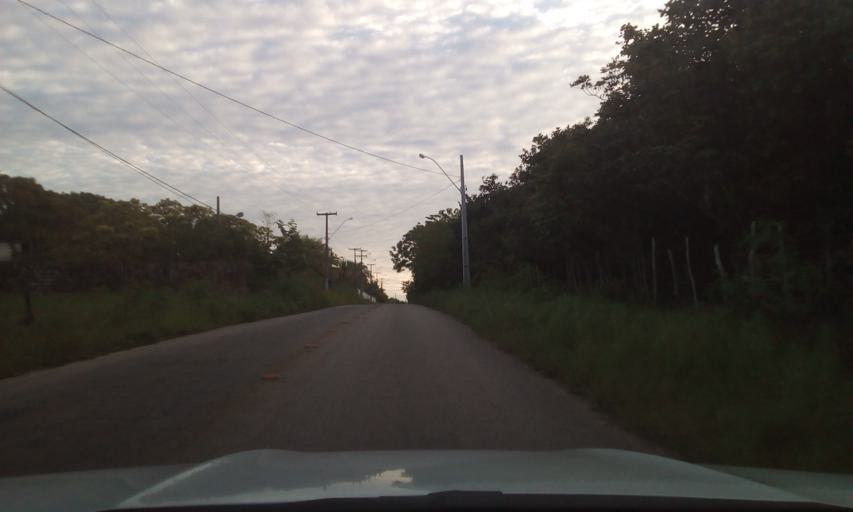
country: BR
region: Paraiba
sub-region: Conde
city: Conde
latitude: -7.2225
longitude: -34.8119
